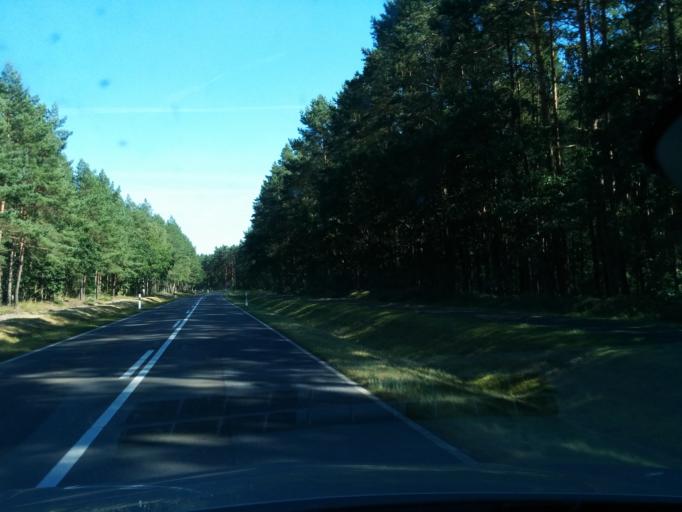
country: DE
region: Mecklenburg-Vorpommern
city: Torgelow
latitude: 53.6355
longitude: 13.9655
